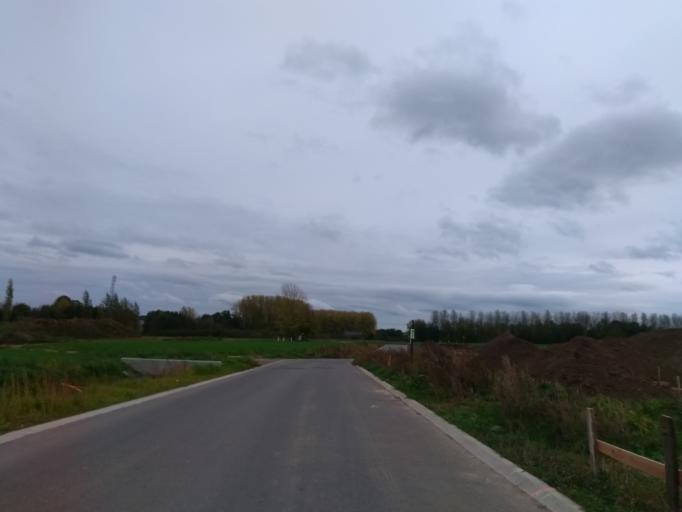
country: BE
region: Flanders
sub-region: Provincie Oost-Vlaanderen
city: Oosterzele
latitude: 50.9327
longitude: 3.7763
